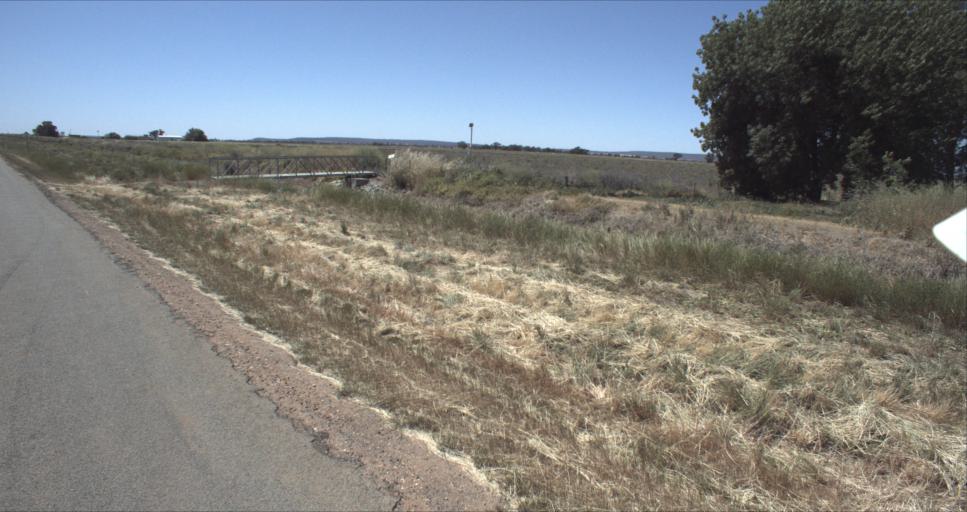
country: AU
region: New South Wales
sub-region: Leeton
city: Leeton
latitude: -34.5110
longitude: 146.3448
